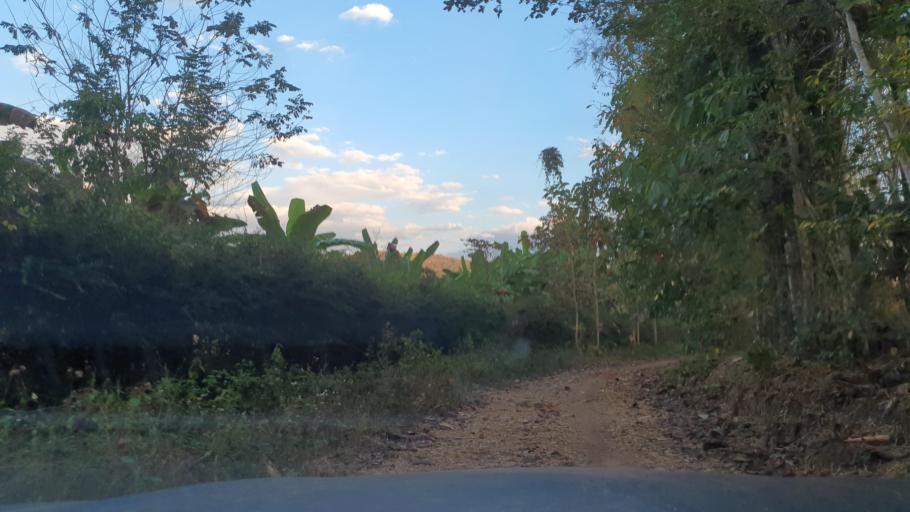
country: TH
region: Chiang Mai
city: Hang Dong
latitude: 18.7320
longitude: 98.8770
